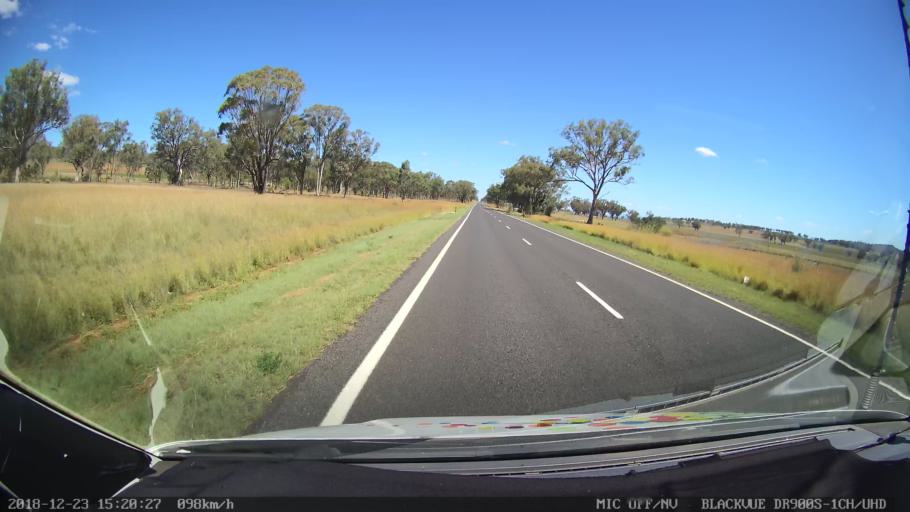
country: AU
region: New South Wales
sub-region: Tamworth Municipality
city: Manilla
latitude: -30.8429
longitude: 150.7899
